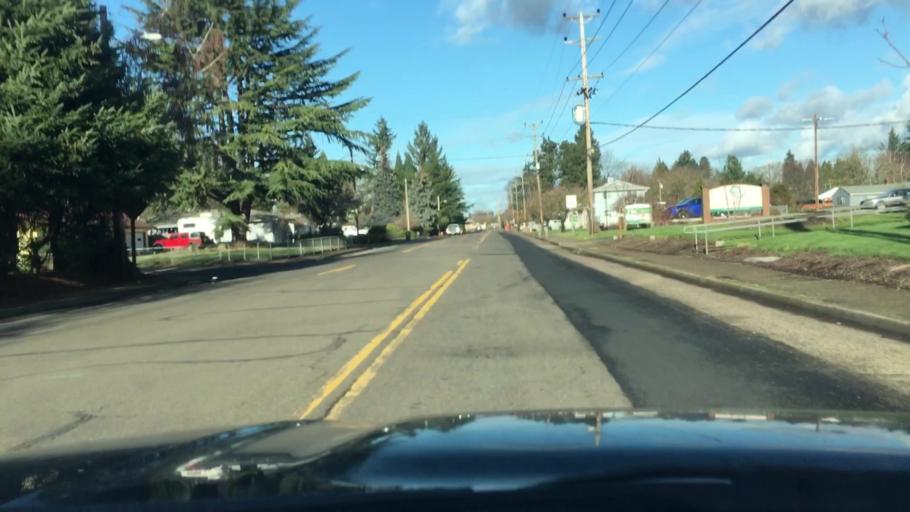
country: US
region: Oregon
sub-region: Lane County
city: Eugene
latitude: 44.0666
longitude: -123.1630
